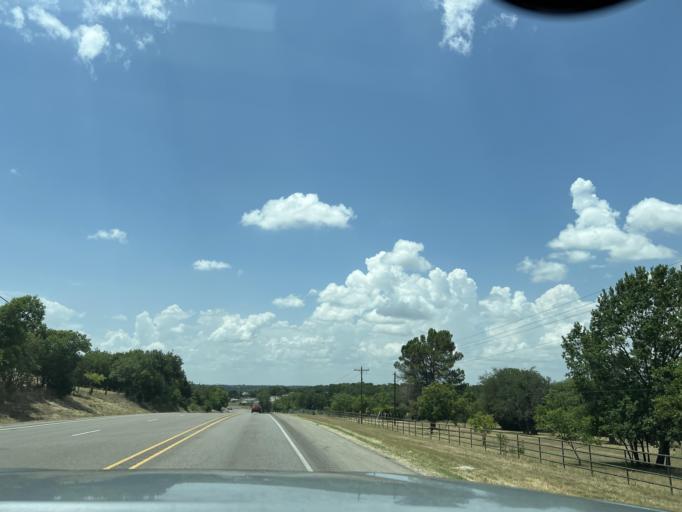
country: US
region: Texas
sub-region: Parker County
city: Weatherford
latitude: 32.8206
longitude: -97.7748
